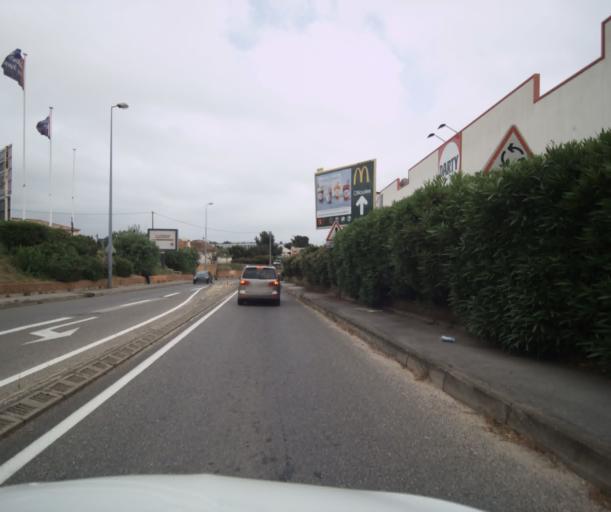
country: FR
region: Provence-Alpes-Cote d'Azur
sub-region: Departement du Var
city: Ollioules
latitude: 43.1279
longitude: 5.8769
